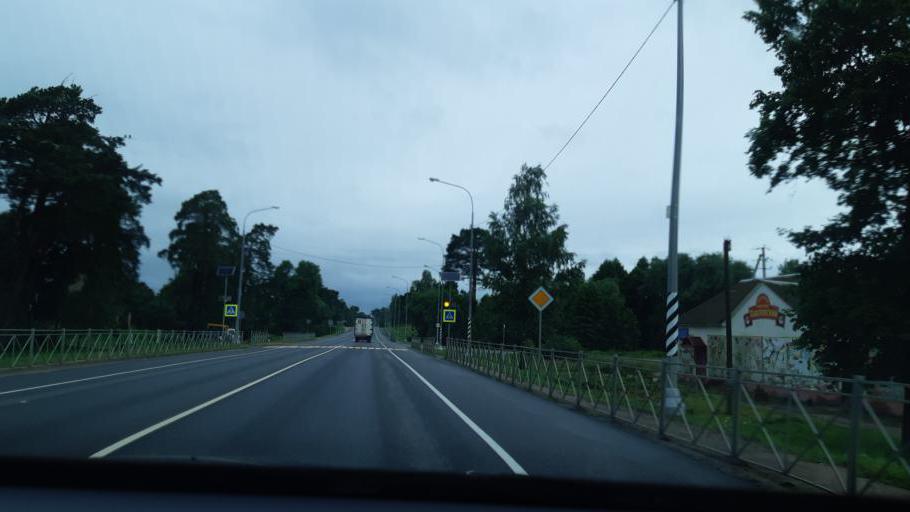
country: RU
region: Smolensk
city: Oster
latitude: 53.9915
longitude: 32.8185
